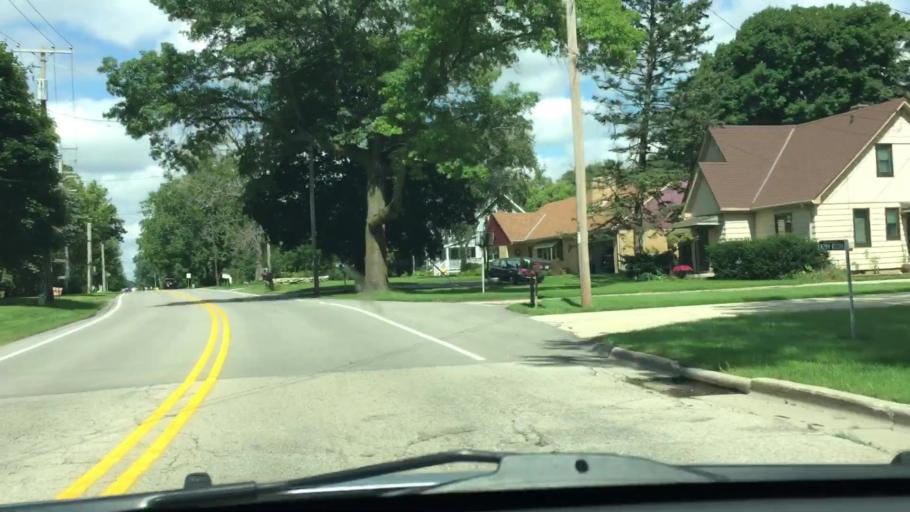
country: US
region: Wisconsin
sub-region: Waukesha County
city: Hartland
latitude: 43.1145
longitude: -88.3430
